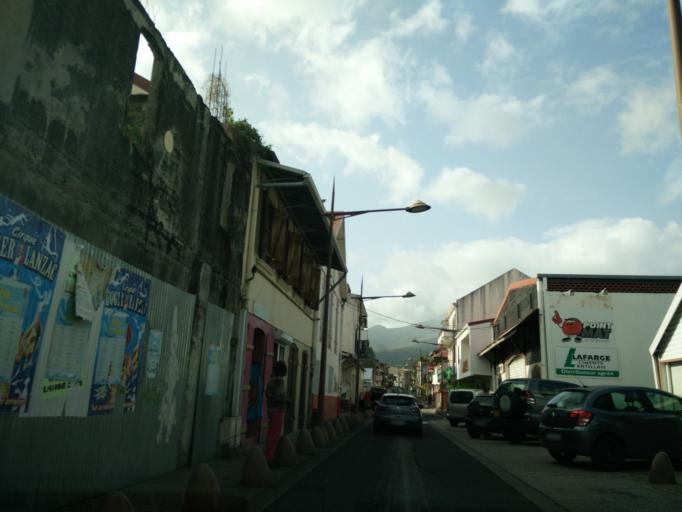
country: MQ
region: Martinique
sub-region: Martinique
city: Saint-Pierre
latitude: 14.7412
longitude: -61.1759
